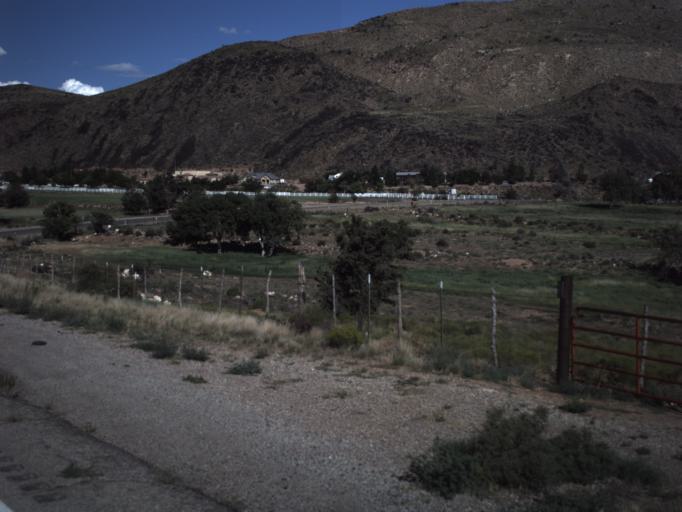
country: US
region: Utah
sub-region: Washington County
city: Toquerville
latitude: 37.2602
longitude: -113.2902
